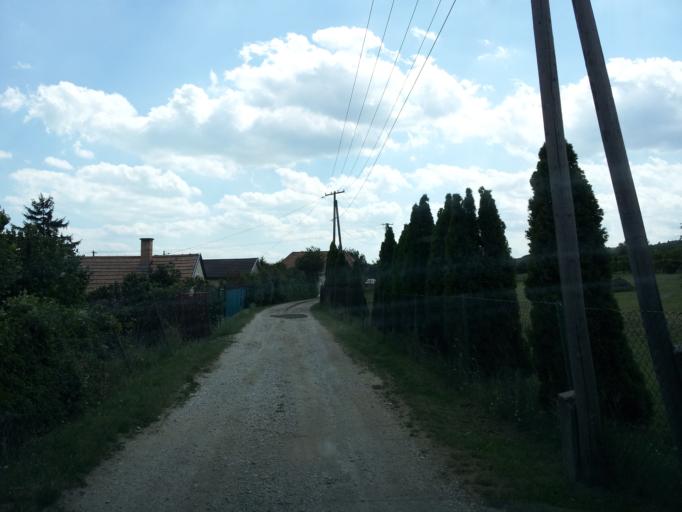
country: HU
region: Veszprem
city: Balatonalmadi
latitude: 47.0615
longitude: 18.0223
